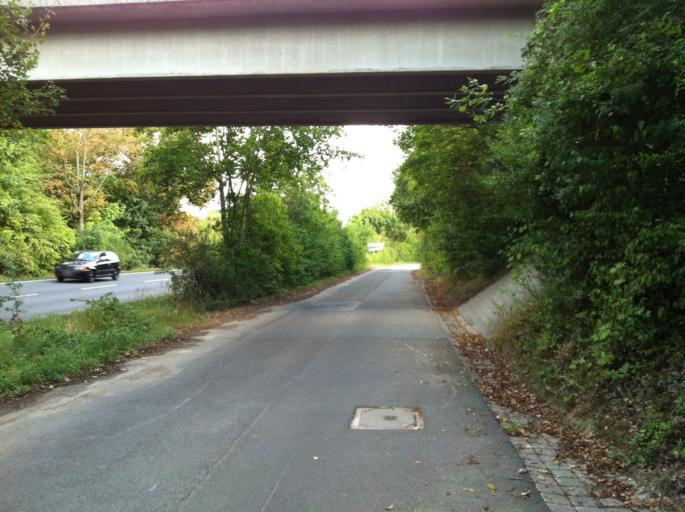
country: DE
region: Rheinland-Pfalz
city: Mainz
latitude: 49.9815
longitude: 8.2335
